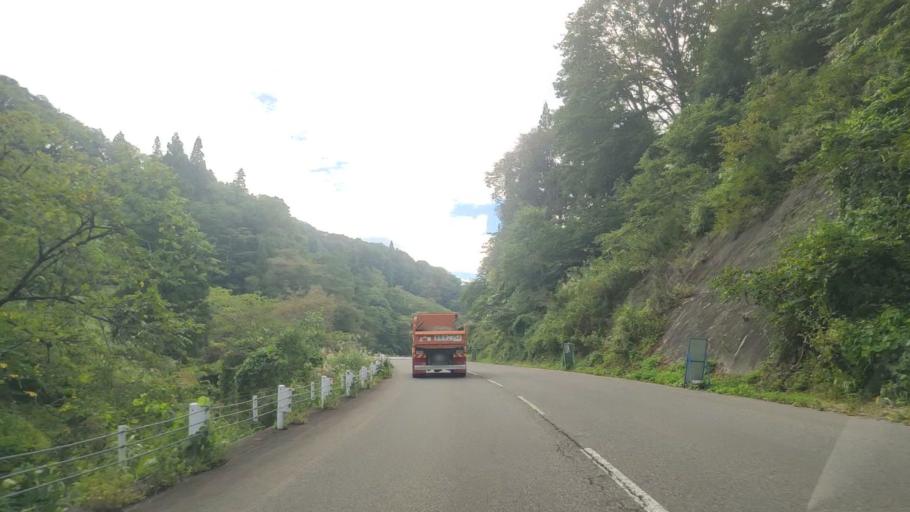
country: JP
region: Nagano
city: Iiyama
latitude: 36.8979
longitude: 138.3197
